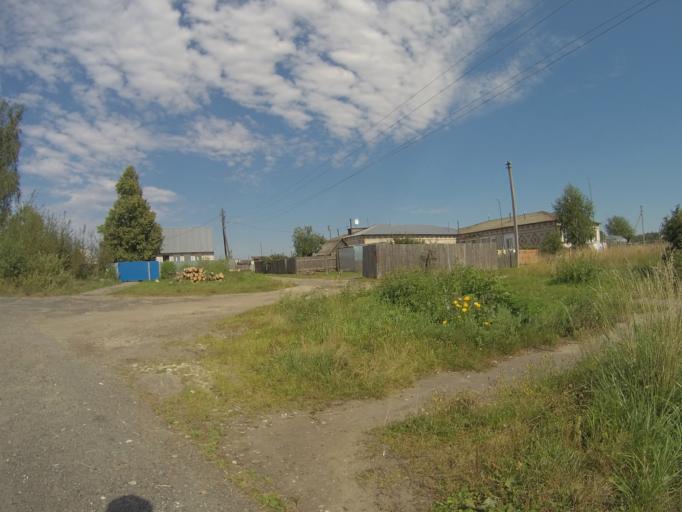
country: RU
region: Vladimir
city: Orgtrud
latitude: 56.0372
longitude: 40.6853
